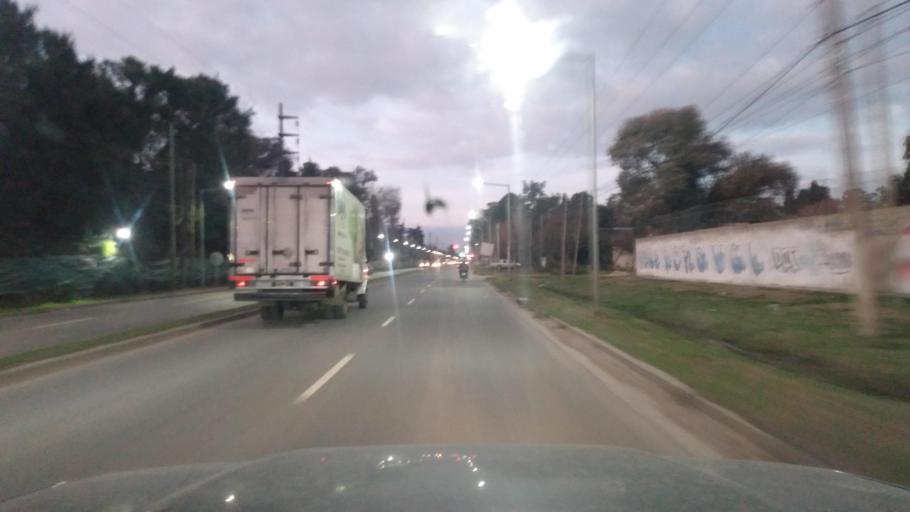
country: AR
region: Buenos Aires
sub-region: Partido de Pilar
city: Pilar
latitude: -34.4411
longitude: -58.8979
